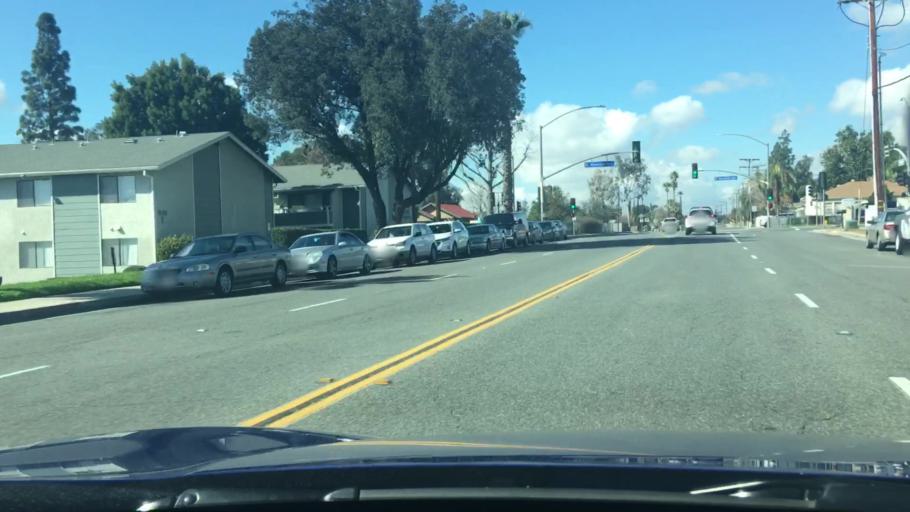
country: US
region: California
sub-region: San Bernardino County
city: Rialto
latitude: 34.0850
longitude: -117.3695
